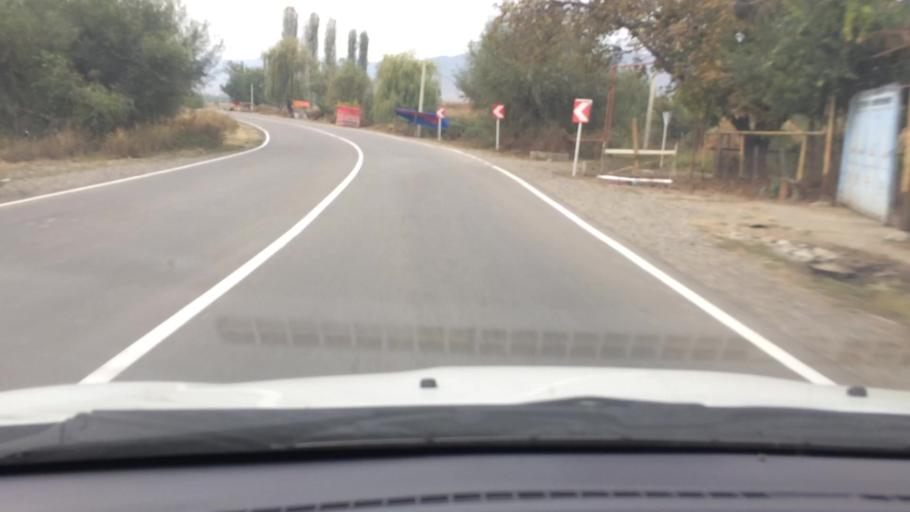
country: GE
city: Naghvarevi
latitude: 41.3228
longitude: 44.7984
